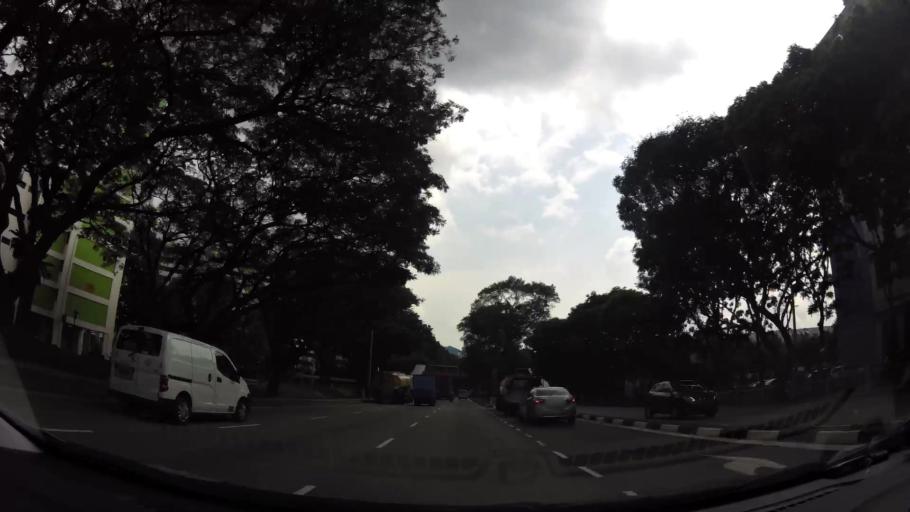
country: SG
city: Singapore
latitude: 1.3056
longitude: 103.7599
